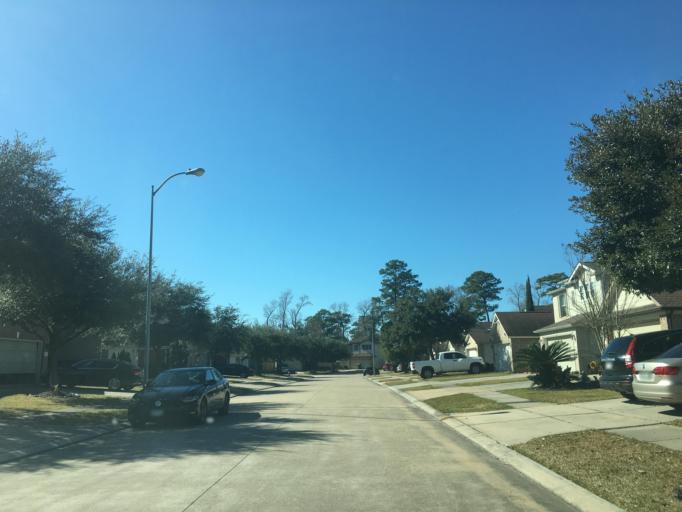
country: US
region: Texas
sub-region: Harris County
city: Spring
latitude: 30.0870
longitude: -95.4637
